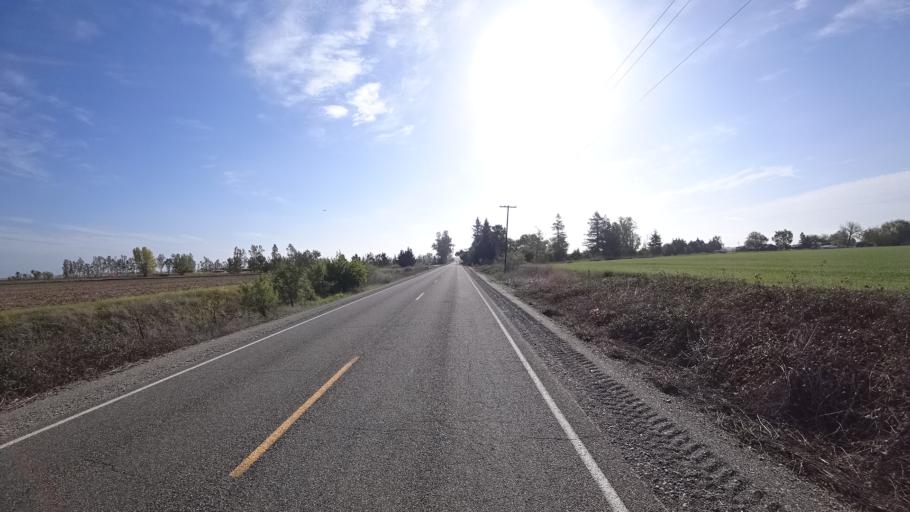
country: US
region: California
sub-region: Glenn County
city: Hamilton City
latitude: 39.5825
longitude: -122.0409
